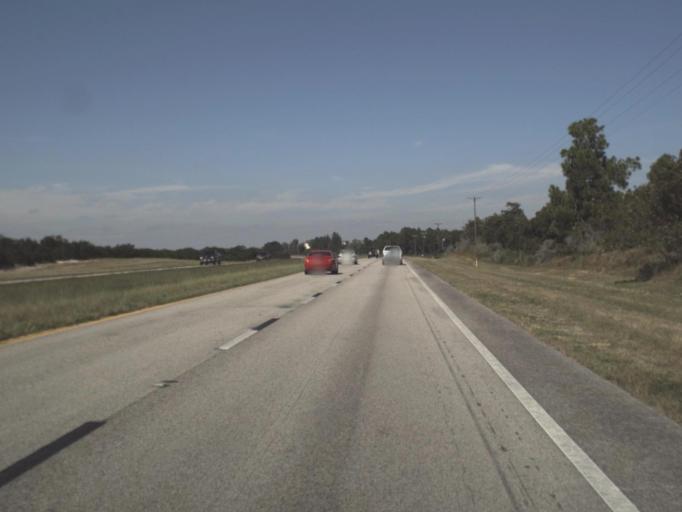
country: US
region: Florida
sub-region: Highlands County
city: Lake Placid
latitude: 27.2250
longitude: -81.3285
